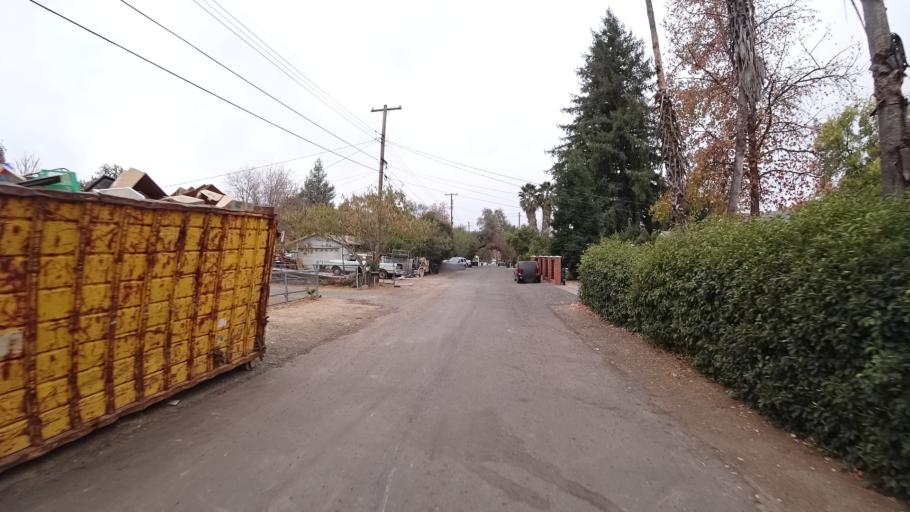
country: US
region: California
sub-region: Sacramento County
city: Citrus Heights
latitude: 38.6992
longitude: -121.2866
